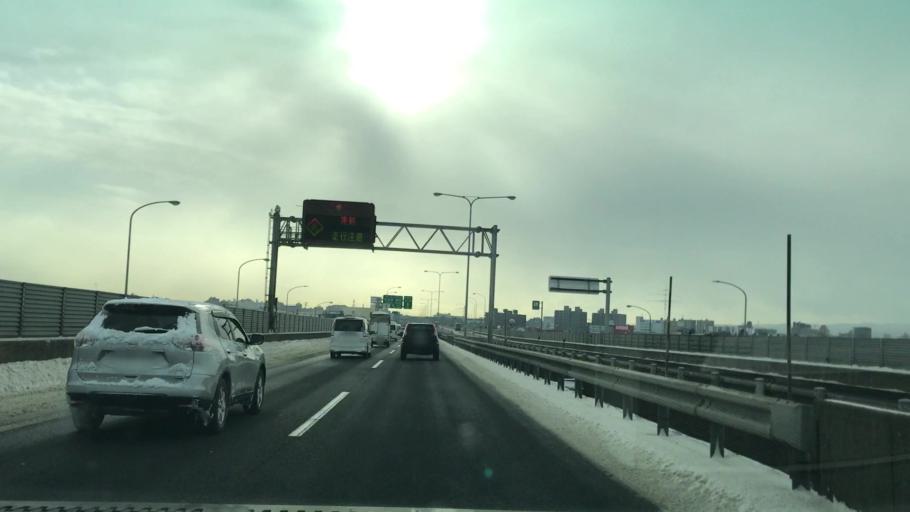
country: JP
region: Hokkaido
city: Sapporo
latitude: 43.0454
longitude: 141.4351
